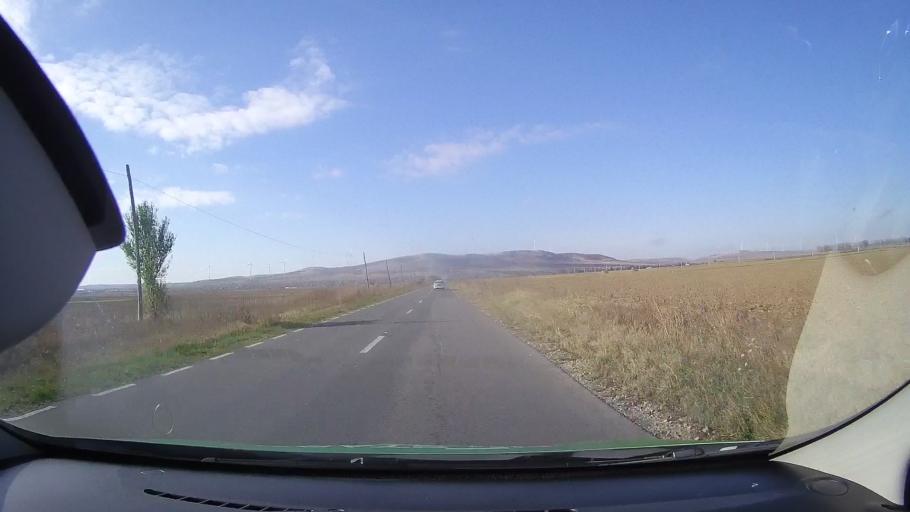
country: RO
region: Tulcea
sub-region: Comuna Valea Nucarilor
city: Agighiol
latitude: 45.0365
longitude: 28.9004
